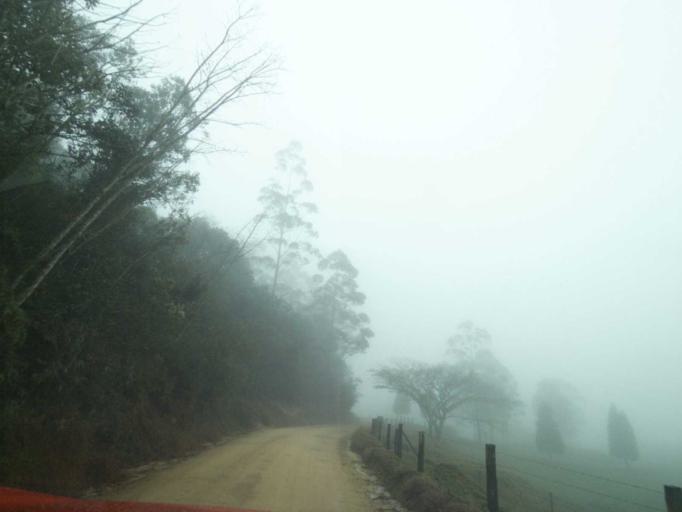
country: BR
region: Santa Catarina
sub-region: Anitapolis
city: Anitapolis
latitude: -27.9197
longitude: -49.1778
